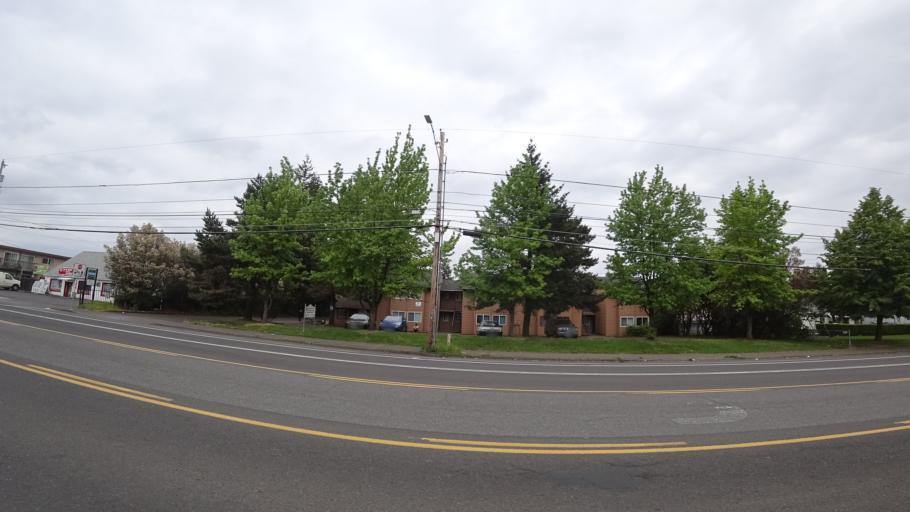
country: US
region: Oregon
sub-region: Multnomah County
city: Lents
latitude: 45.5075
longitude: -122.5379
